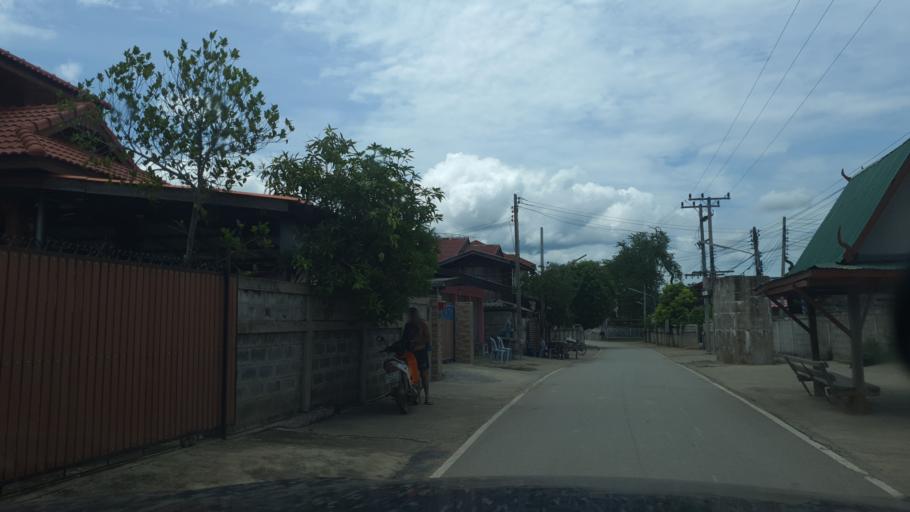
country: TH
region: Lampang
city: Sop Prap
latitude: 17.8800
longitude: 99.3833
